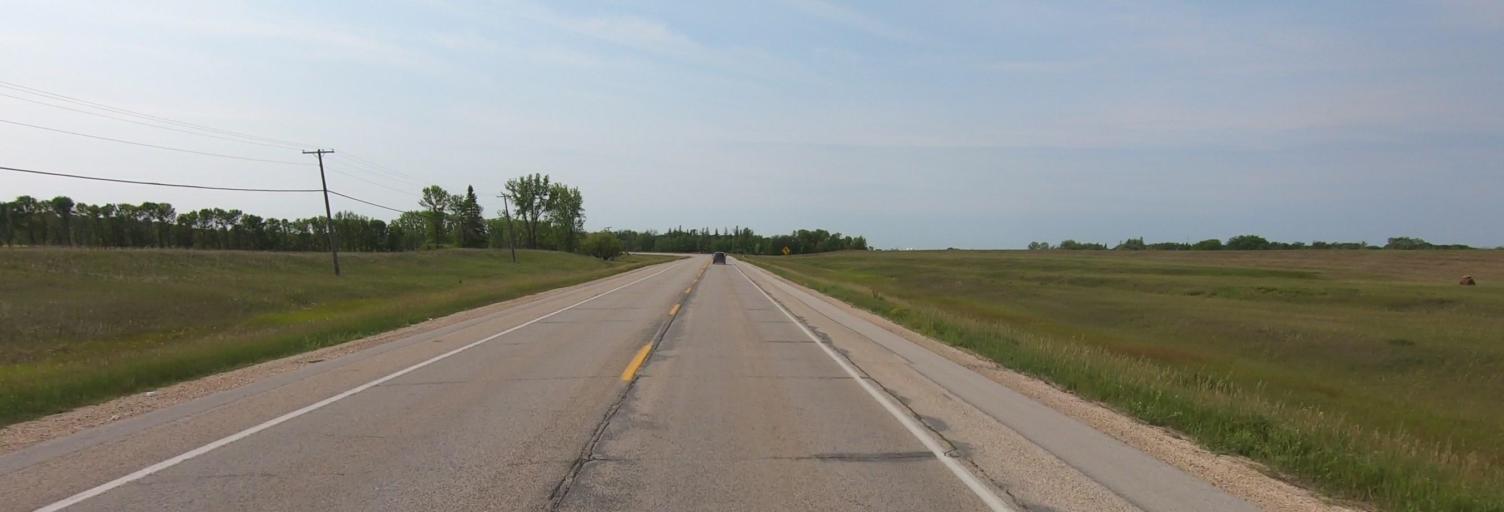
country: CA
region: Manitoba
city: Winnipeg
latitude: 49.7462
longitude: -97.1206
